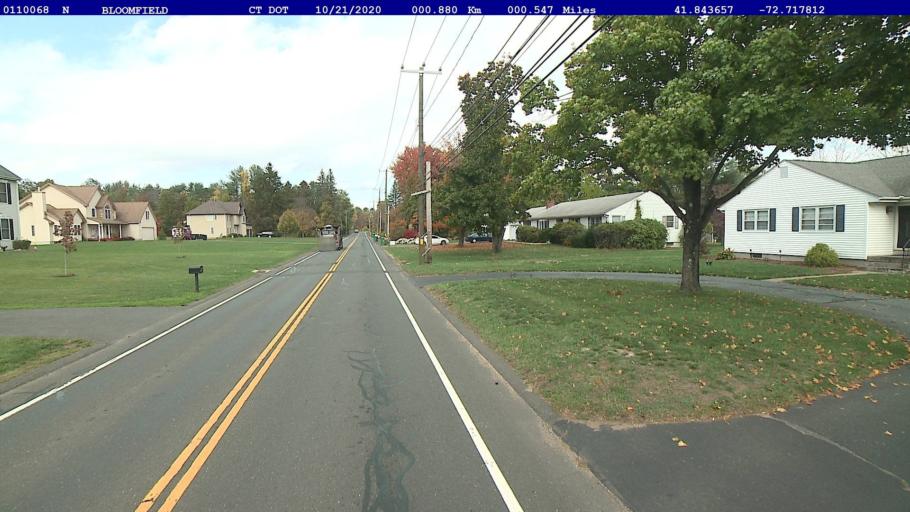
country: US
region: Connecticut
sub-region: Hartford County
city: Blue Hills
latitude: 41.8437
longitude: -72.7178
